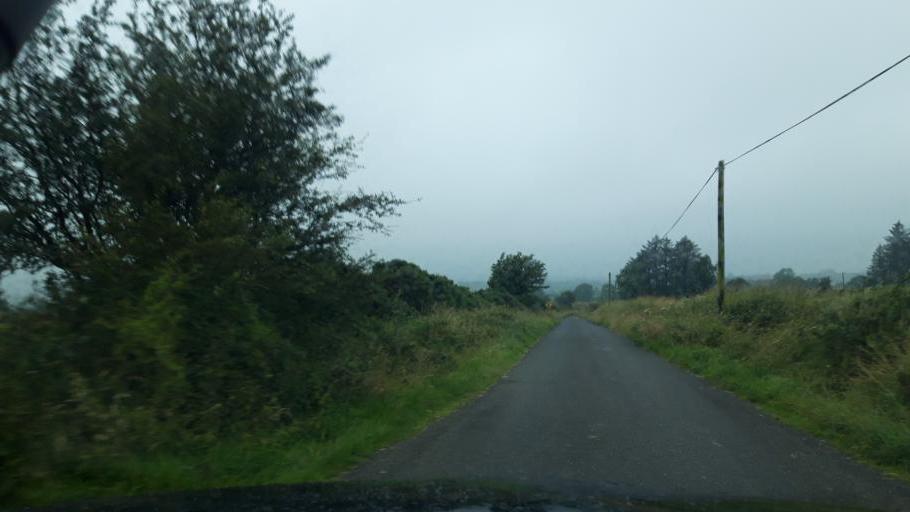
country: IE
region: Leinster
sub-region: Kilkenny
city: Callan
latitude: 52.6357
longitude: -7.5338
